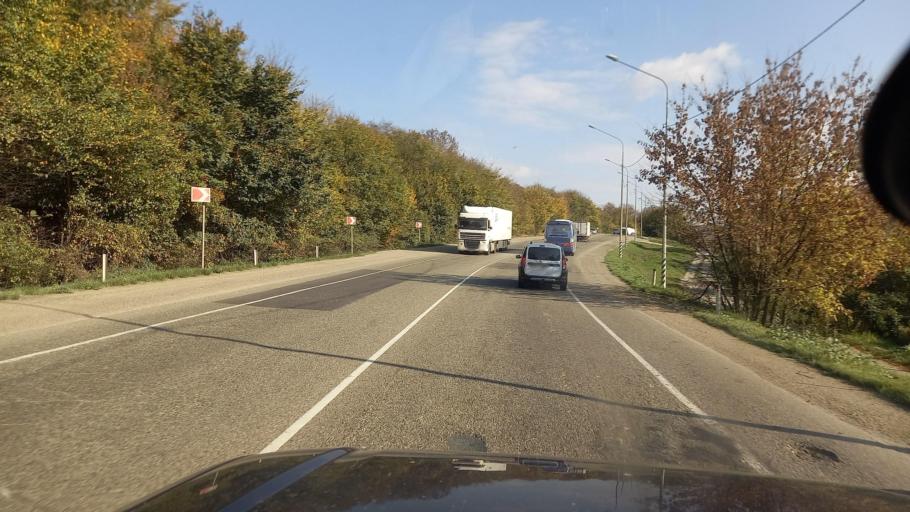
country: RU
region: Krasnodarskiy
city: Verkhnebakanskiy
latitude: 44.8619
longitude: 37.7372
